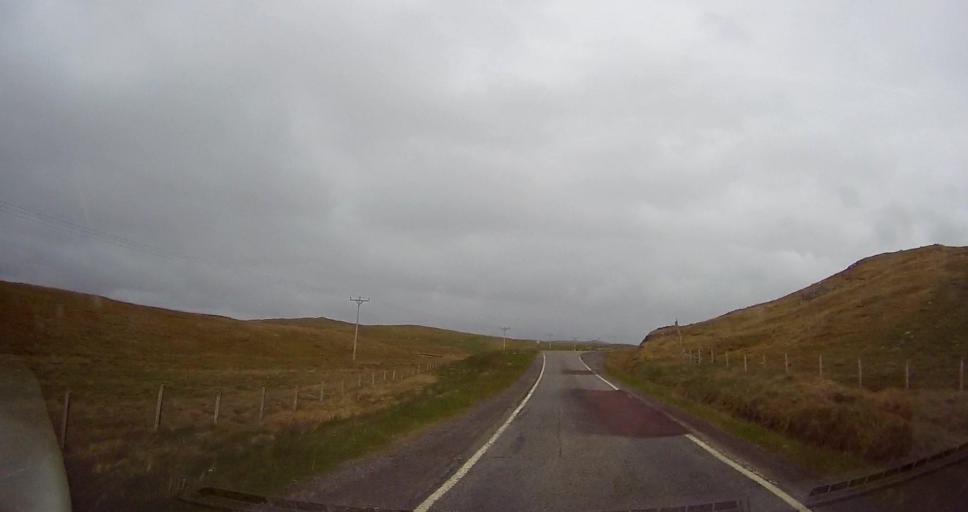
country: GB
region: Scotland
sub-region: Shetland Islands
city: Sandwick
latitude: 60.2358
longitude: -1.5478
